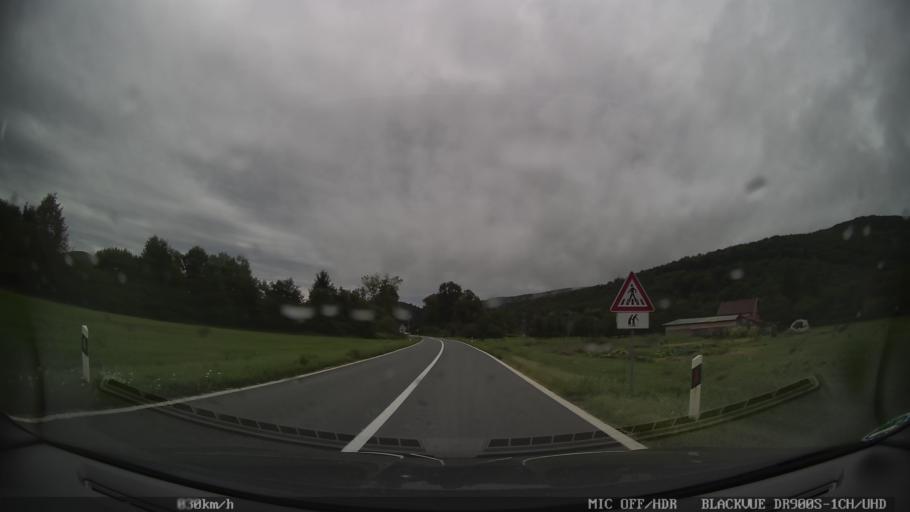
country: HR
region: Licko-Senjska
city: Brinje
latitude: 44.9408
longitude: 15.1257
